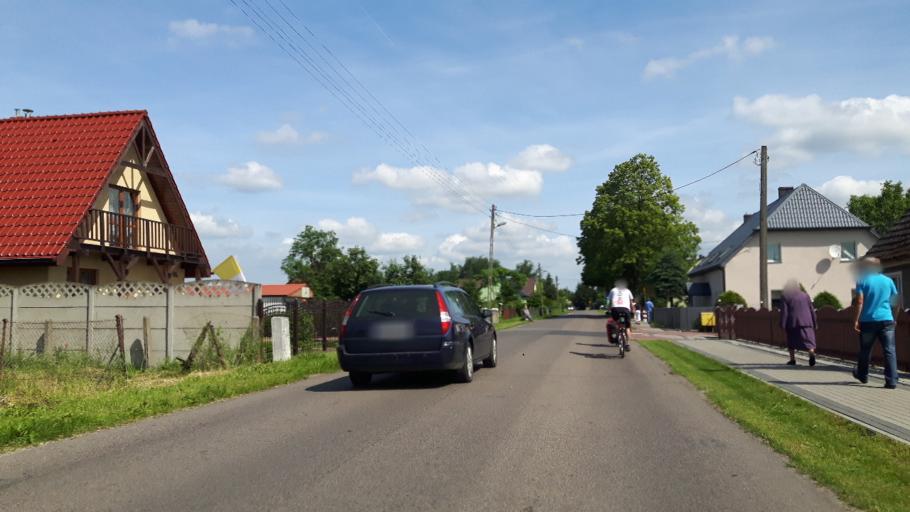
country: PL
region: West Pomeranian Voivodeship
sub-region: Powiat goleniowski
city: Goleniow
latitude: 53.4854
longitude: 14.7762
